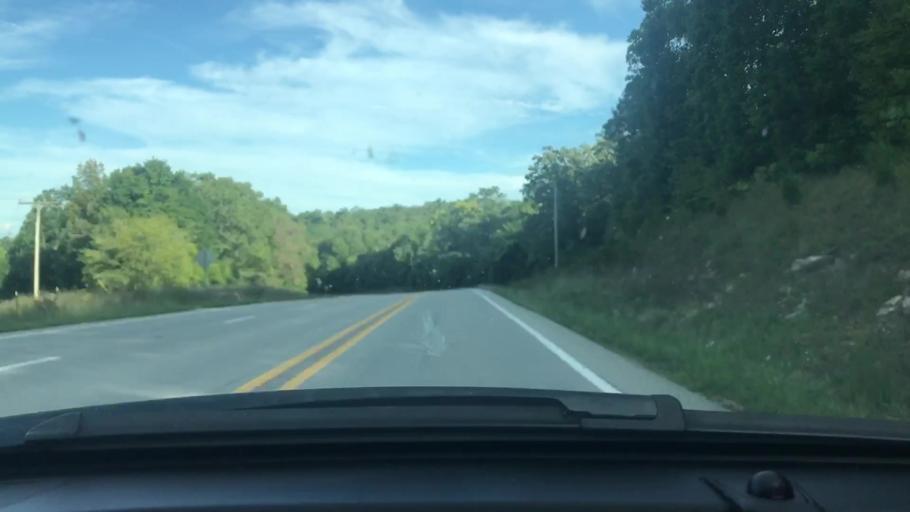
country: US
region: Arkansas
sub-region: Sharp County
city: Cherokee Village
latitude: 36.2740
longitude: -91.3573
